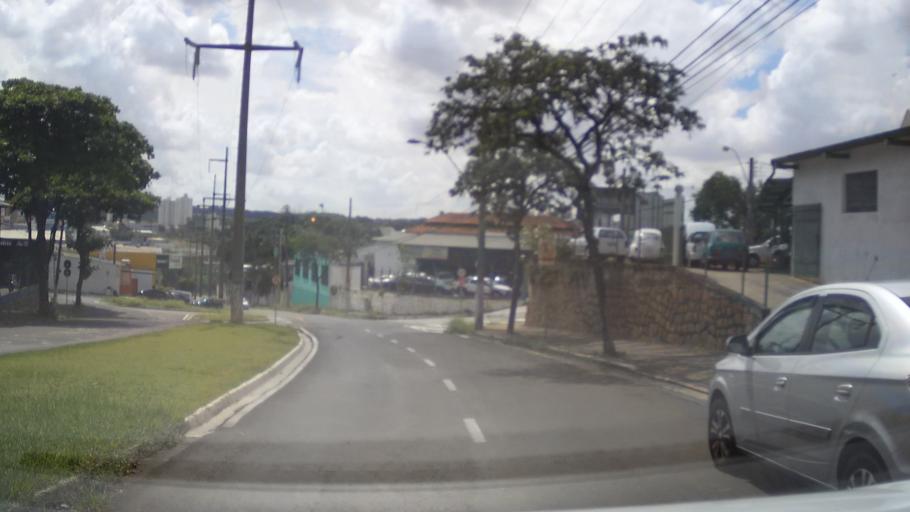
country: BR
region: Sao Paulo
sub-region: Valinhos
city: Valinhos
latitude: -22.9671
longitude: -46.9904
